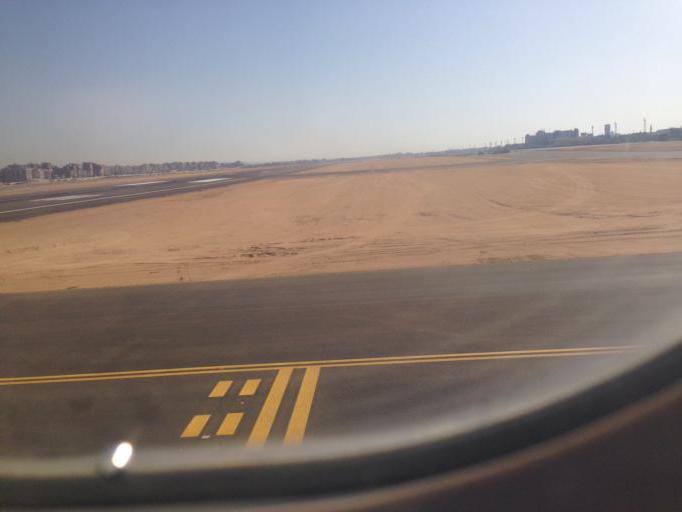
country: EG
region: Muhafazat al Qalyubiyah
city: Al Khankah
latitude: 30.1200
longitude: 31.3821
